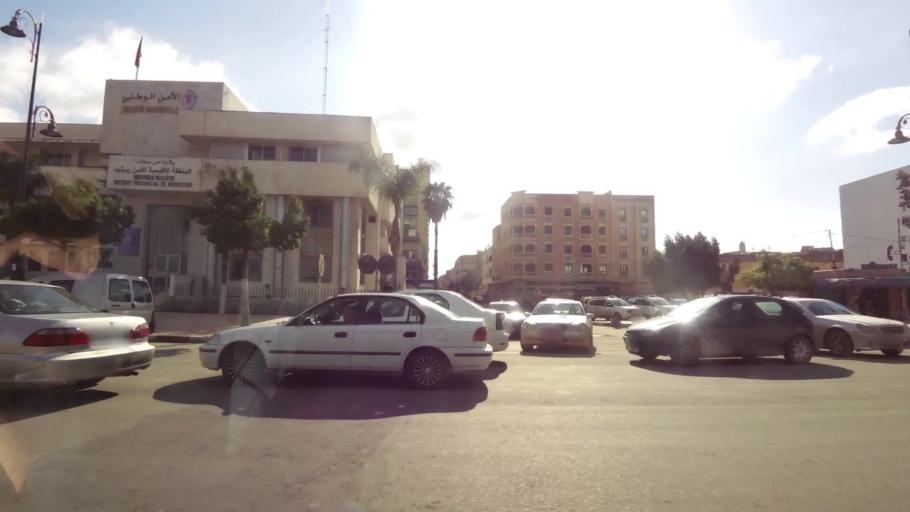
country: MA
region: Chaouia-Ouardigha
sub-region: Settat Province
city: Berrechid
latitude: 33.2658
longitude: -7.5834
